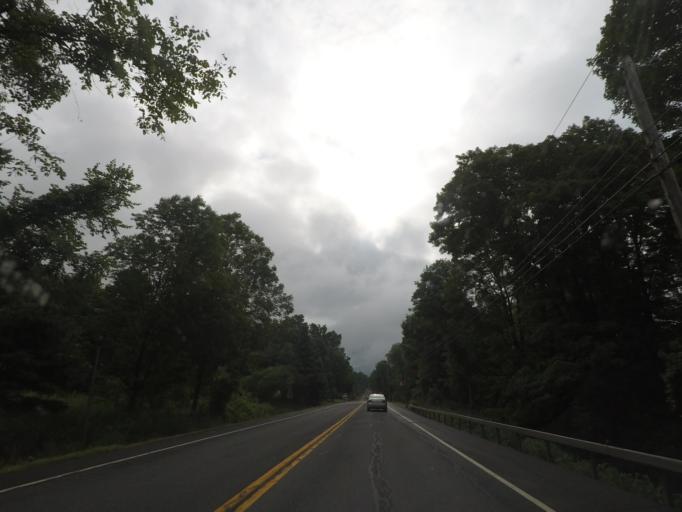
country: US
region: New York
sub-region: Rensselaer County
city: Nassau
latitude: 42.4960
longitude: -73.5202
